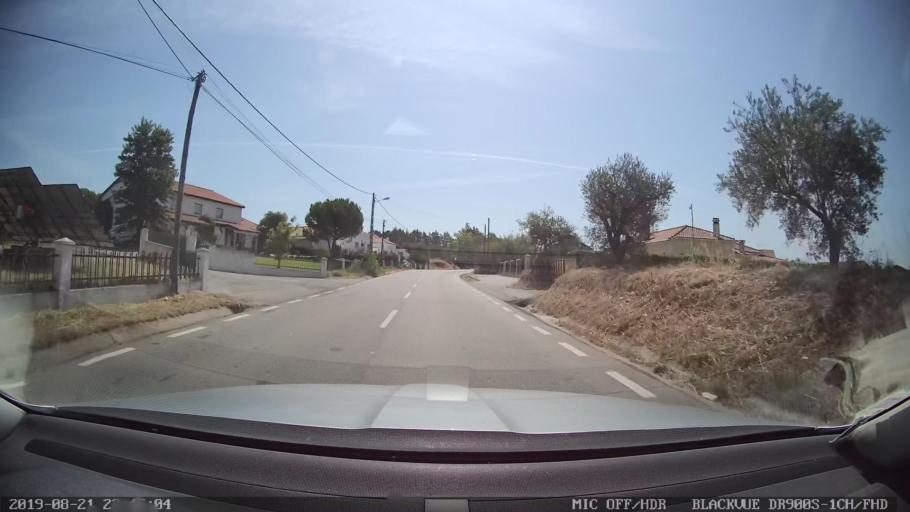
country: PT
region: Castelo Branco
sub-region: Idanha-A-Nova
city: Idanha-a-Nova
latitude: 39.8417
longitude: -7.2685
